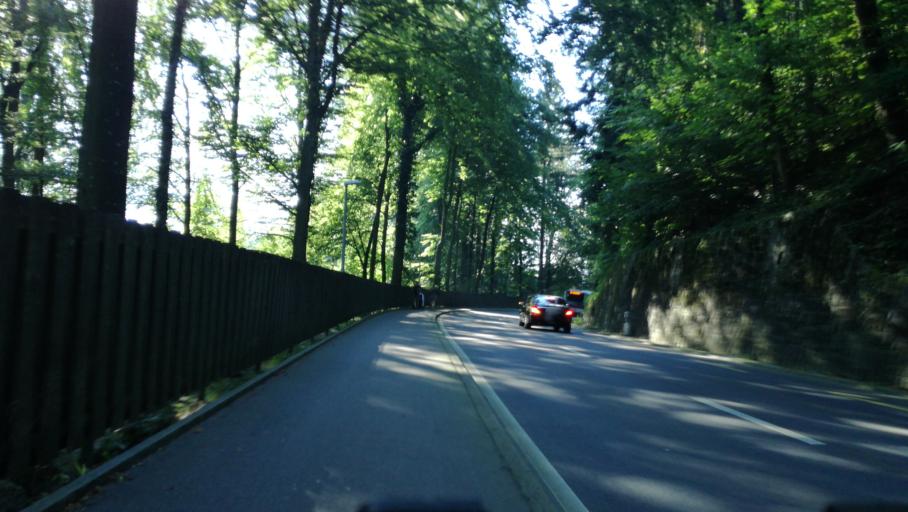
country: CH
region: Lucerne
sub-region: Lucerne-Land District
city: Meierskappel
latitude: 47.1370
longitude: 8.4645
